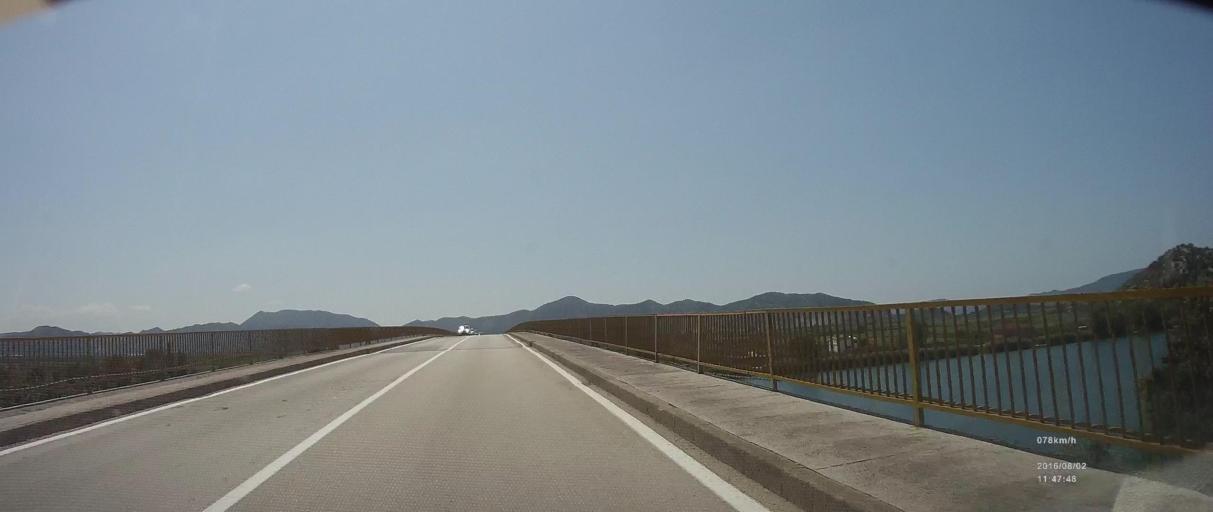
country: HR
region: Dubrovacko-Neretvanska
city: Komin
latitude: 43.0397
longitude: 17.4843
